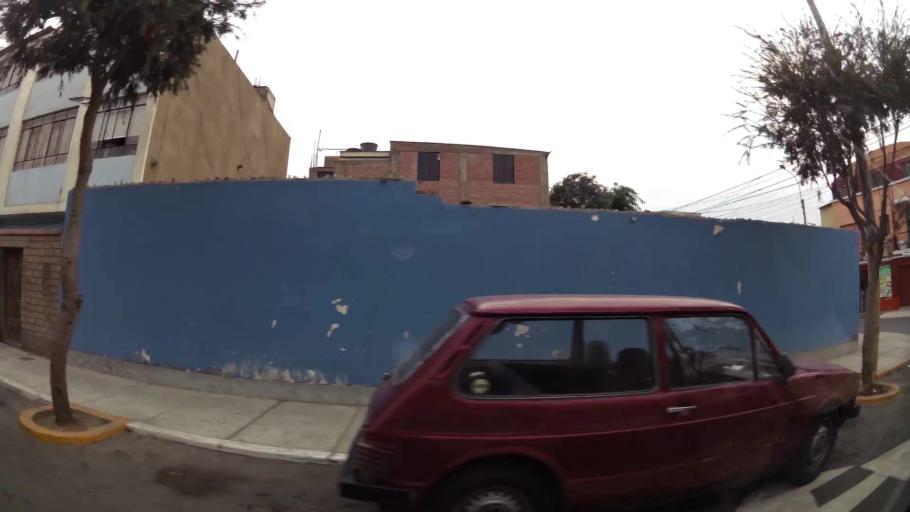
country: PE
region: Lima
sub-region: Lima
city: Surco
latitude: -12.1373
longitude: -77.0205
